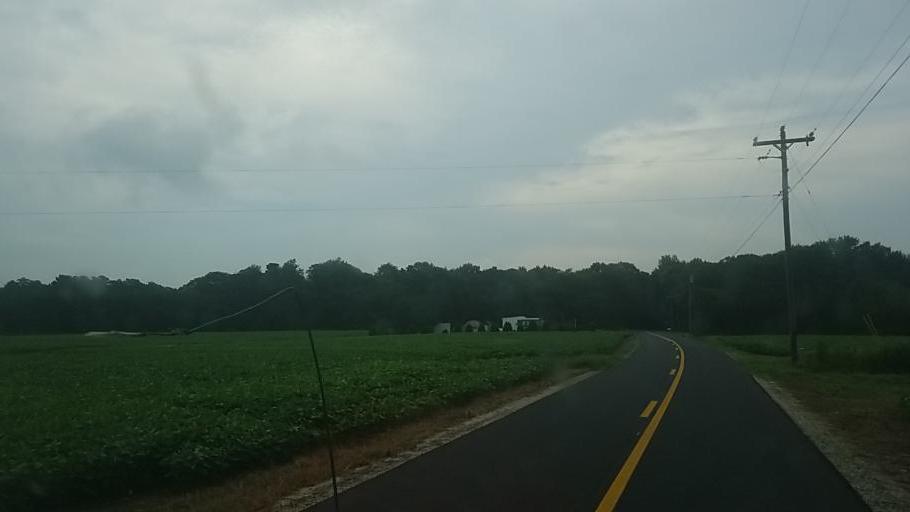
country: US
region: Delaware
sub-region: Sussex County
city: Selbyville
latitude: 38.4370
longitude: -75.2521
